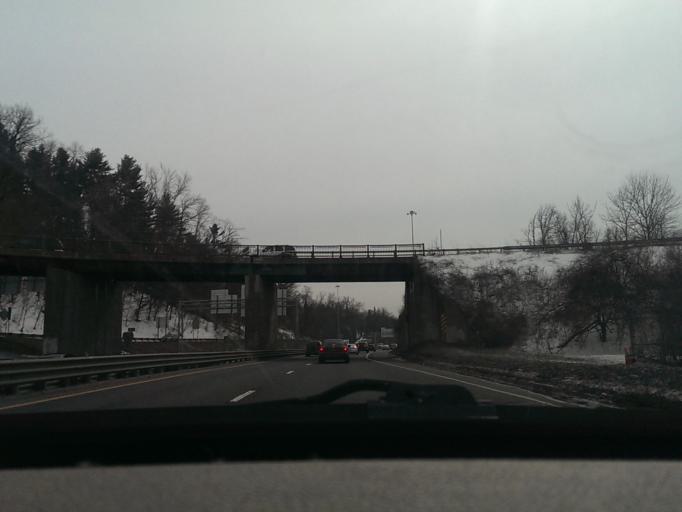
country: US
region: Massachusetts
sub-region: Hampden County
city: Springfield
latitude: 42.0827
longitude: -72.5792
